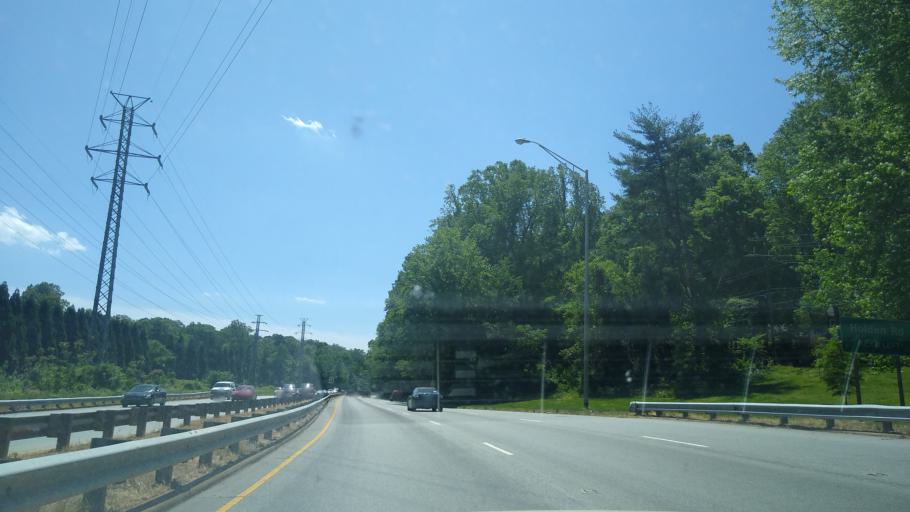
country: US
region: North Carolina
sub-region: Guilford County
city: Greensboro
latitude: 36.0690
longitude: -79.8415
